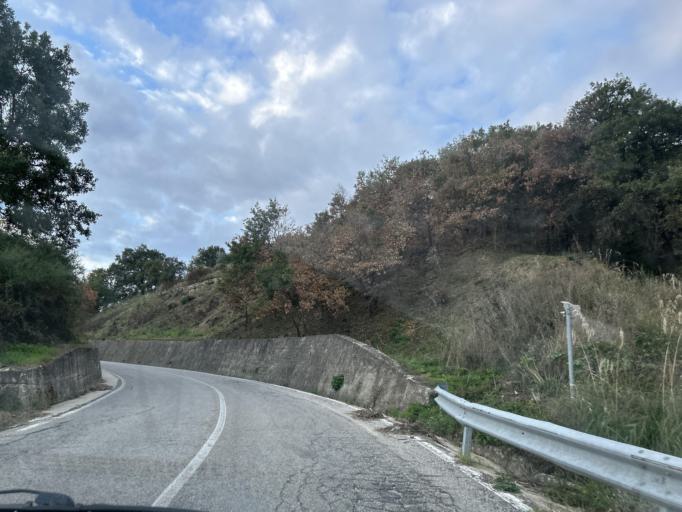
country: IT
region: Calabria
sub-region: Provincia di Catanzaro
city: Montauro
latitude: 38.7474
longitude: 16.5090
